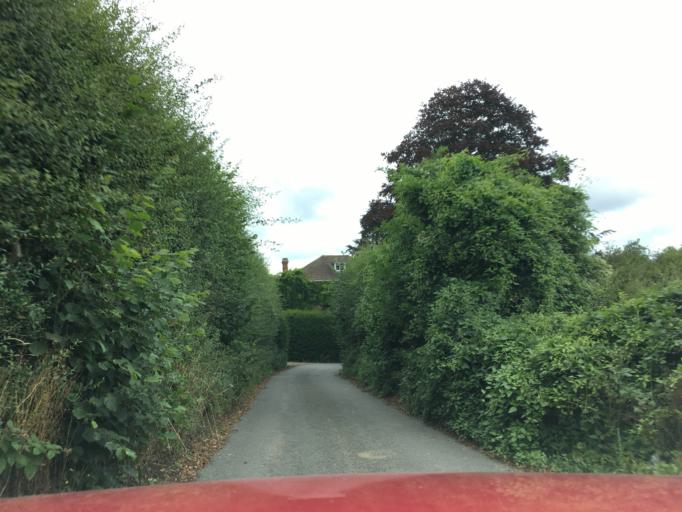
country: GB
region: England
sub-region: Kent
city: Maidstone
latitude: 51.2354
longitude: 0.5424
